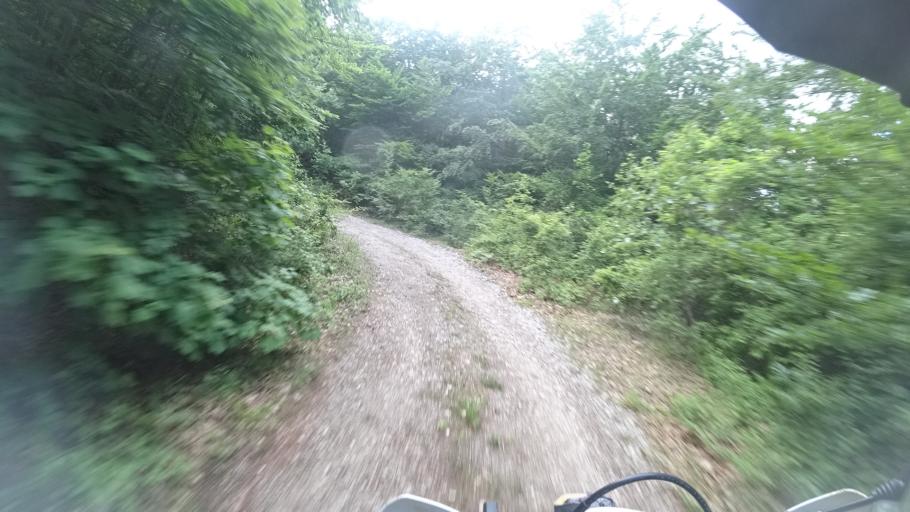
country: HR
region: Zadarska
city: Gracac
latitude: 44.2627
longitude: 15.9322
